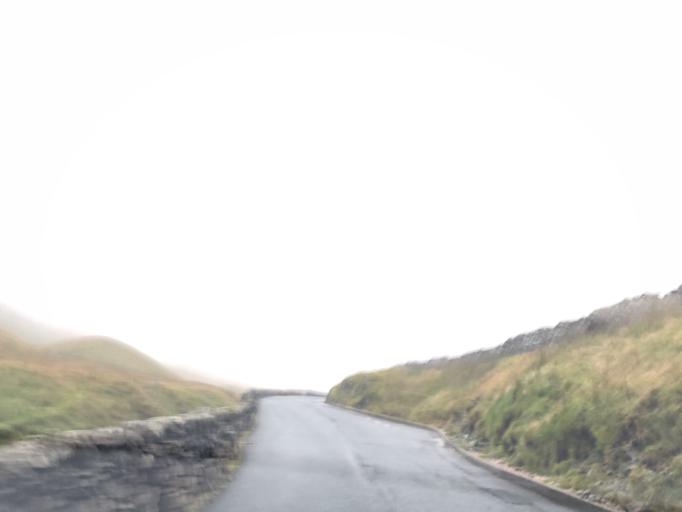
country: GB
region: England
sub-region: Cumbria
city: Ambleside
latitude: 54.4708
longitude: -2.9232
